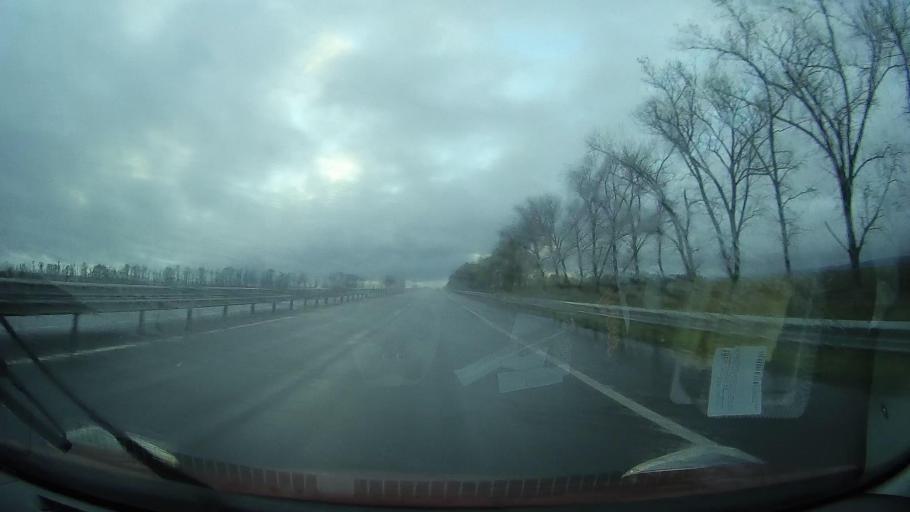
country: RU
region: Stavropol'skiy
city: Zavetnoye
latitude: 44.7866
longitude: 41.5131
